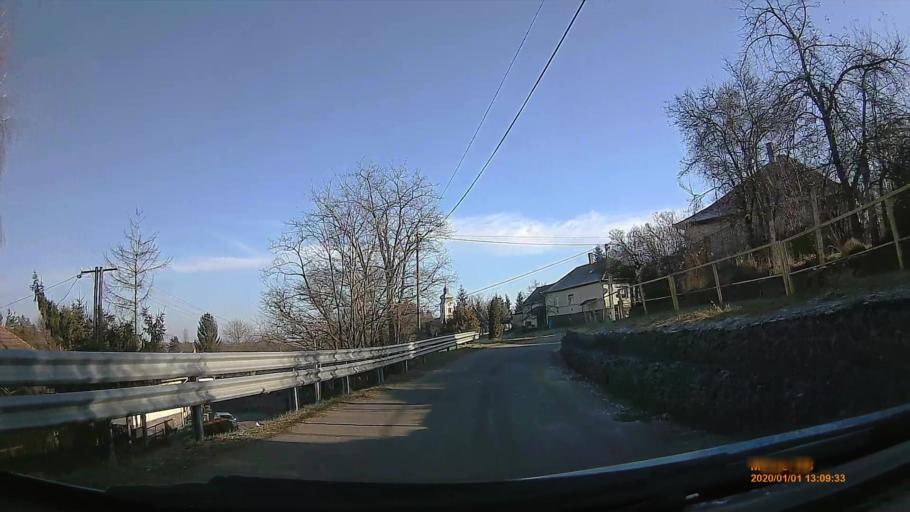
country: HU
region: Heves
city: Parad
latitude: 47.9446
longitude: 20.0187
